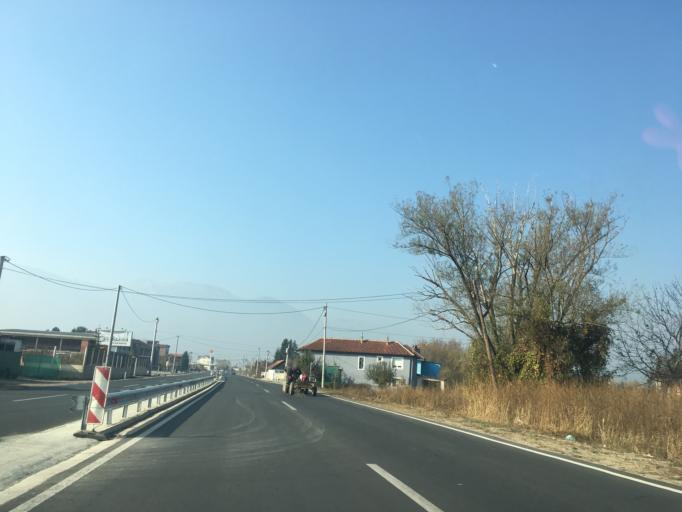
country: XK
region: Pec
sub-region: Komuna e Pejes
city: Dubova (Driloni)
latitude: 42.6593
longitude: 20.3607
